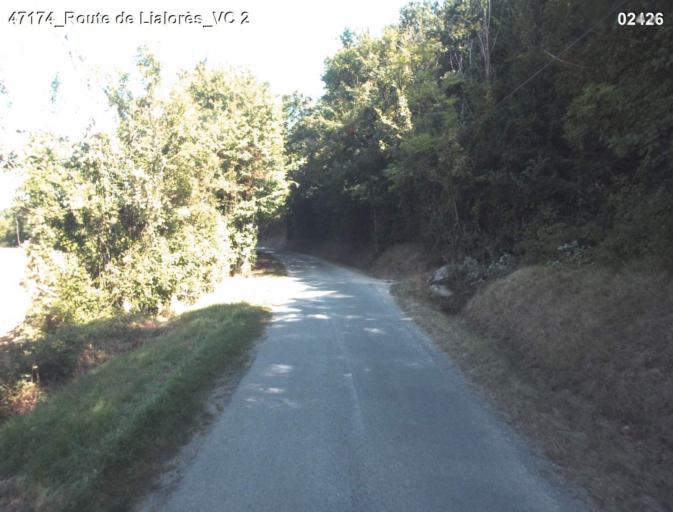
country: FR
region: Midi-Pyrenees
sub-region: Departement du Gers
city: Condom
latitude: 44.0250
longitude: 0.3699
